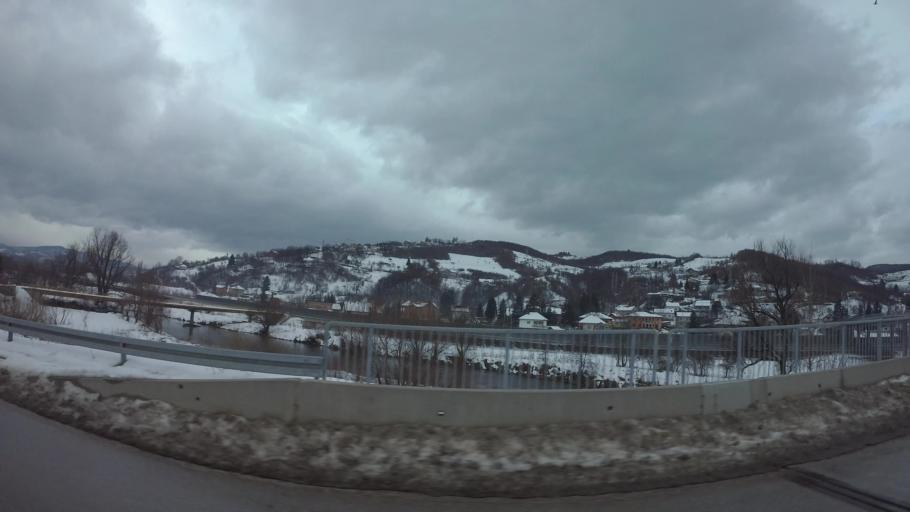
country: BA
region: Federation of Bosnia and Herzegovina
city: Vogosca
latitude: 43.8824
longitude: 18.3066
